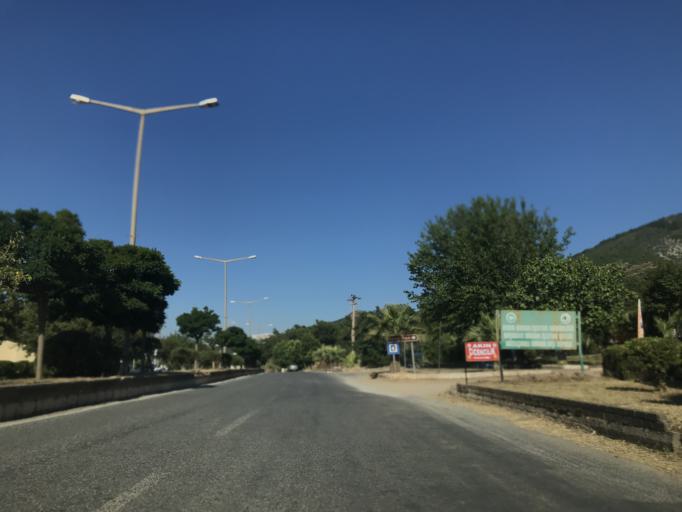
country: TR
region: Aydin
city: Davutlar
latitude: 37.7157
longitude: 27.2324
